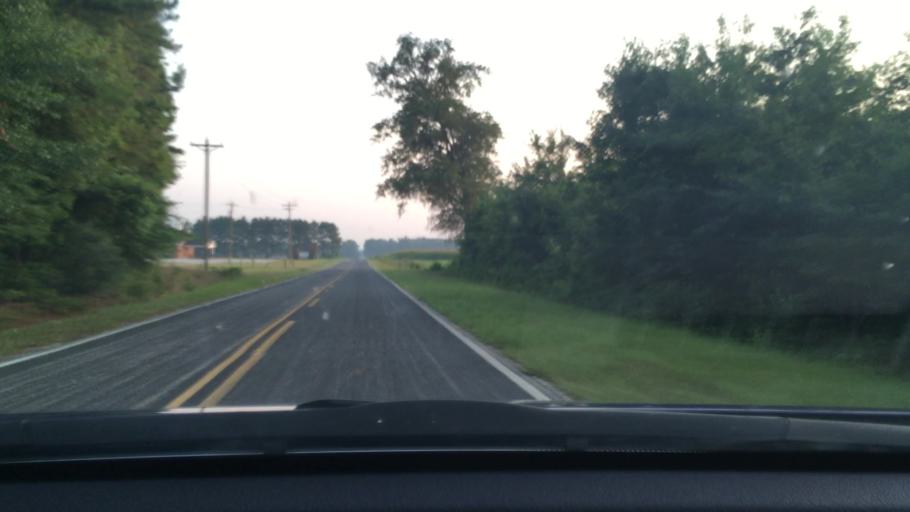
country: US
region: South Carolina
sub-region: Lee County
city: Bishopville
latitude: 34.2470
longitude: -80.1335
